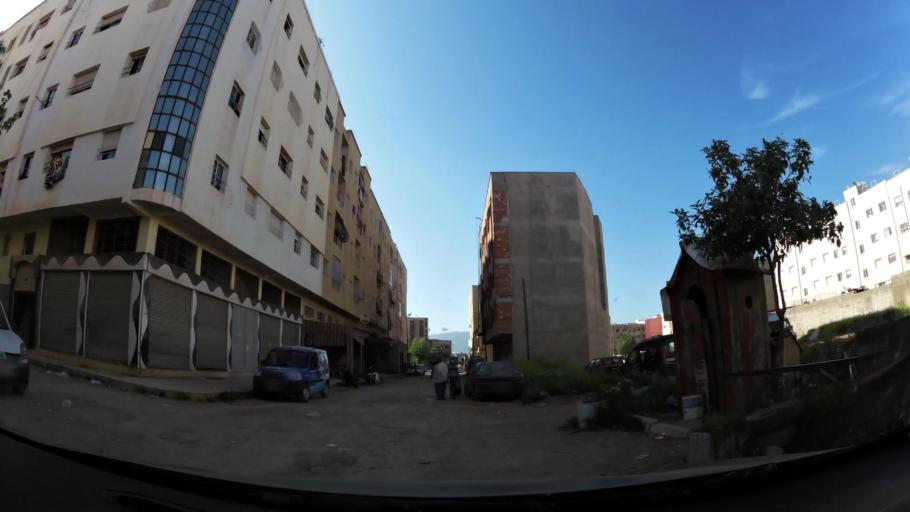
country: MA
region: Fes-Boulemane
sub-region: Fes
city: Fes
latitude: 34.0217
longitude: -5.0372
